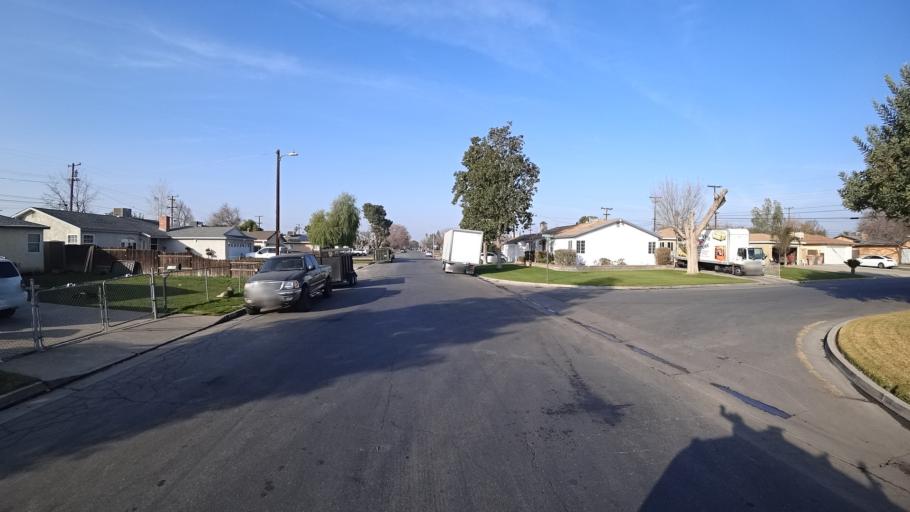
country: US
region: California
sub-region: Kern County
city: Bakersfield
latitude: 35.3370
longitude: -119.0249
